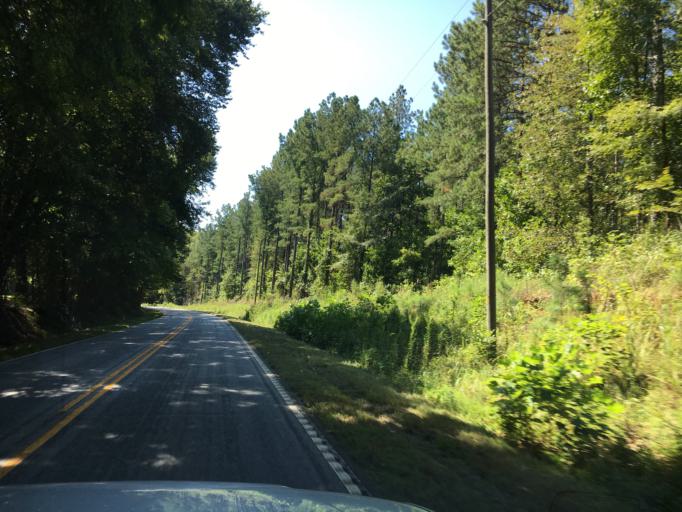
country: US
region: South Carolina
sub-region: Laurens County
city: Clinton
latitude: 34.4213
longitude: -81.8688
